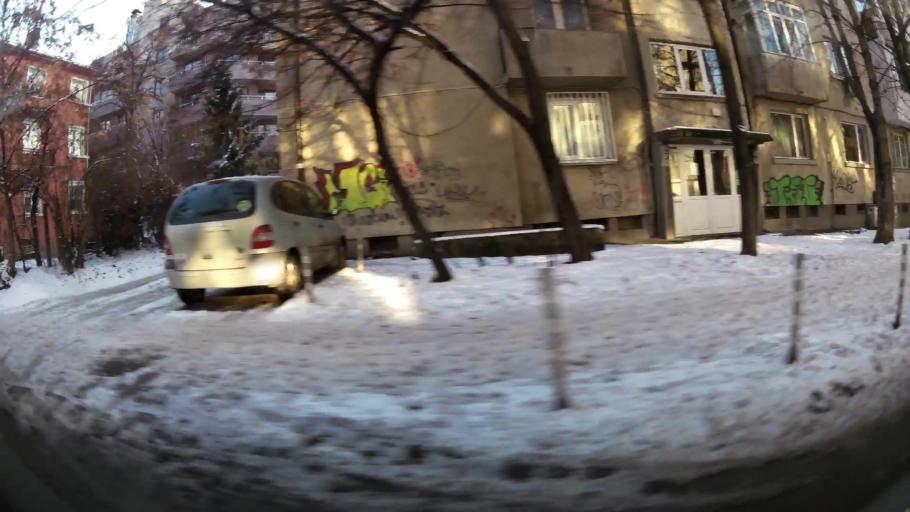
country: BG
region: Sofia-Capital
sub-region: Stolichna Obshtina
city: Sofia
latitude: 42.6858
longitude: 23.3548
